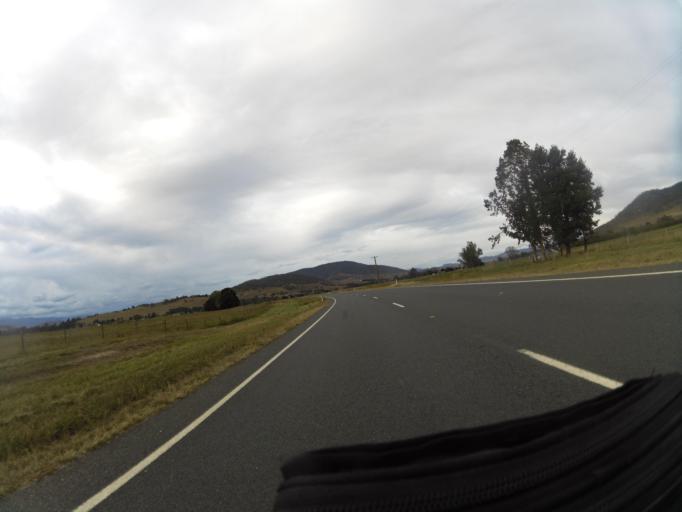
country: AU
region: New South Wales
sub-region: Snowy River
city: Jindabyne
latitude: -36.1135
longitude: 147.9794
